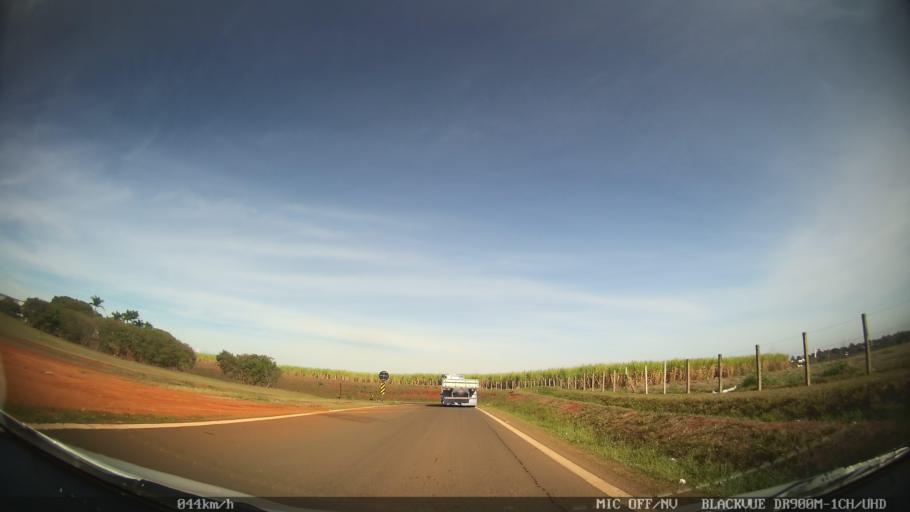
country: BR
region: Sao Paulo
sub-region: Piracicaba
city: Piracicaba
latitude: -22.7808
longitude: -47.6532
